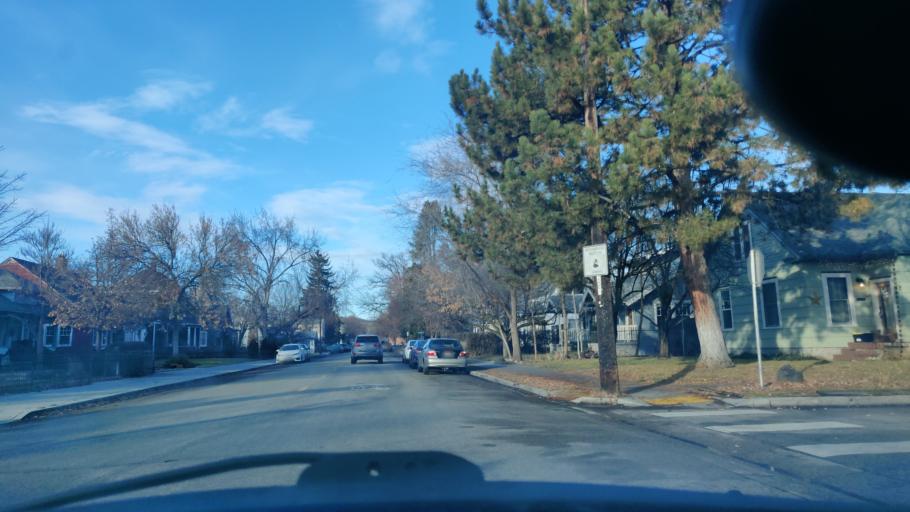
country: US
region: Idaho
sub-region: Ada County
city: Boise
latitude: 43.6274
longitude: -116.2034
